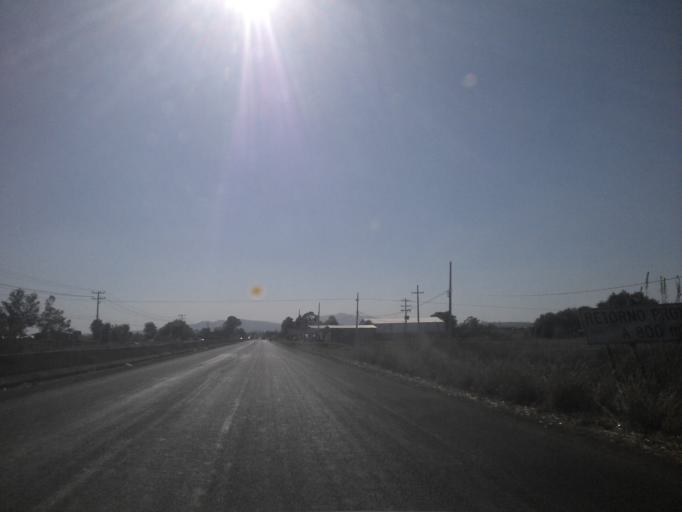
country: MX
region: Jalisco
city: Arandas
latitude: 20.7089
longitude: -102.3921
